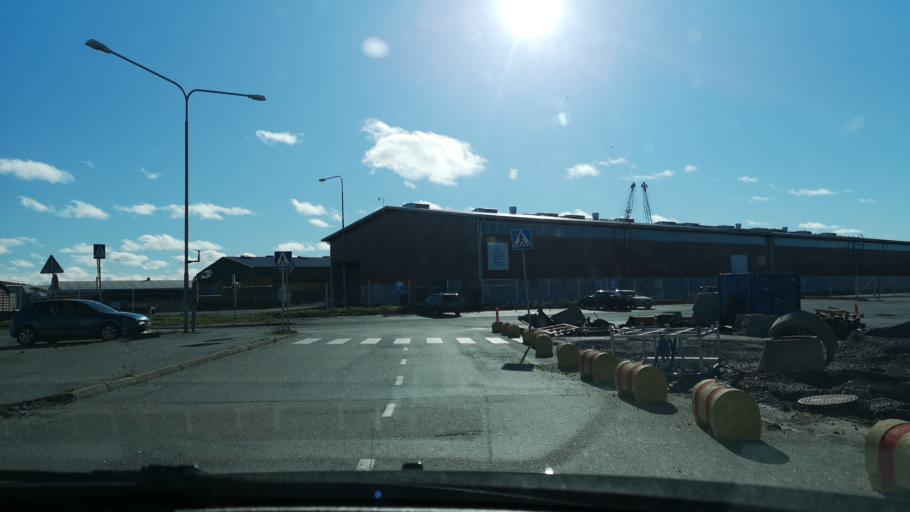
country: FI
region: Ostrobothnia
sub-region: Vaasa
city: Vaasa
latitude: 63.0883
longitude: 21.5598
